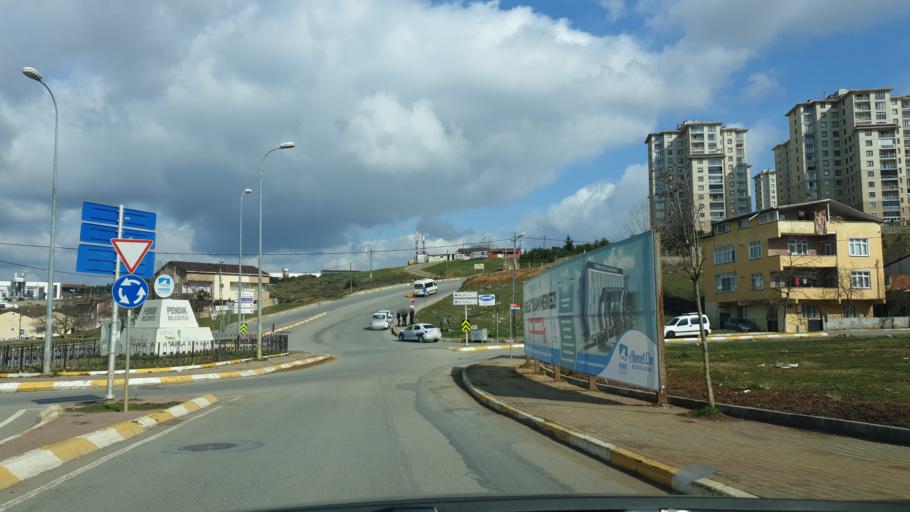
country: TR
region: Istanbul
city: Icmeler
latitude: 40.8682
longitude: 29.3120
